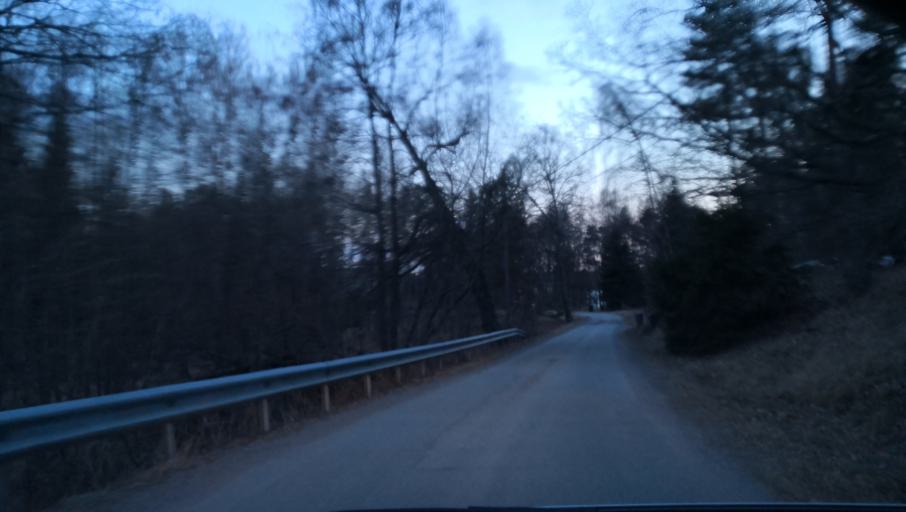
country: SE
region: Stockholm
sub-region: Nacka Kommun
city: Boo
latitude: 59.3261
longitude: 18.3277
